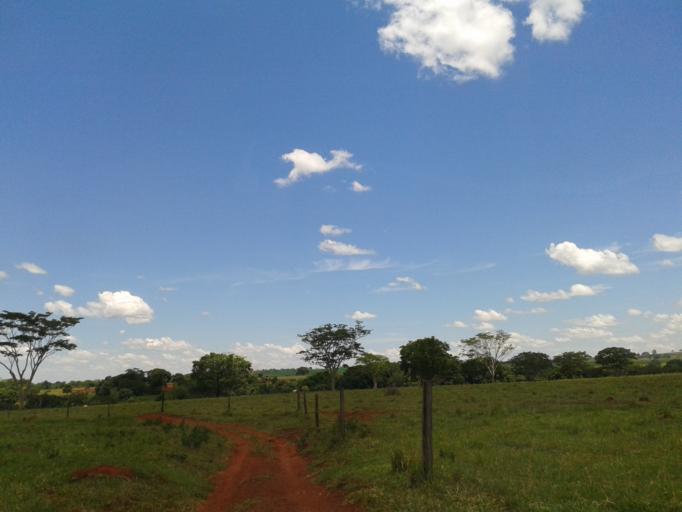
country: BR
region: Minas Gerais
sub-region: Centralina
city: Centralina
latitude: -18.7052
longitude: -49.1762
